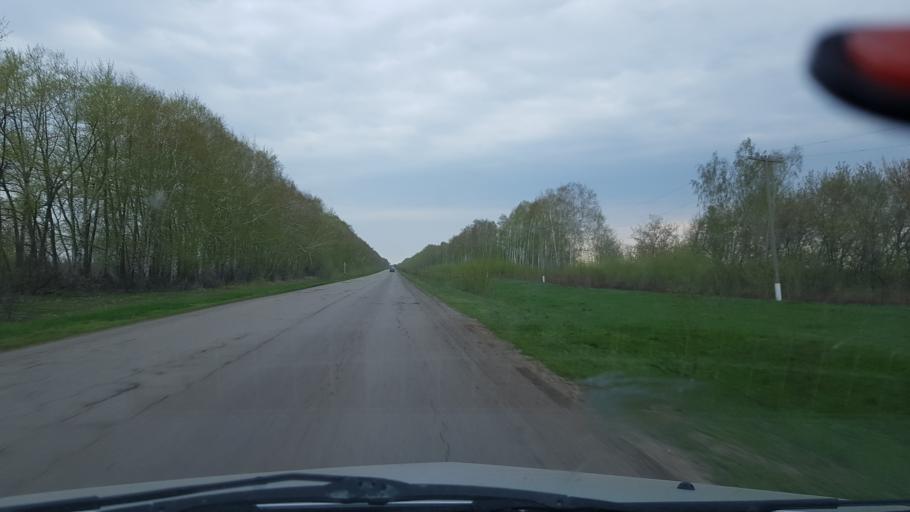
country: RU
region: Samara
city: Podstepki
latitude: 53.6614
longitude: 49.2106
